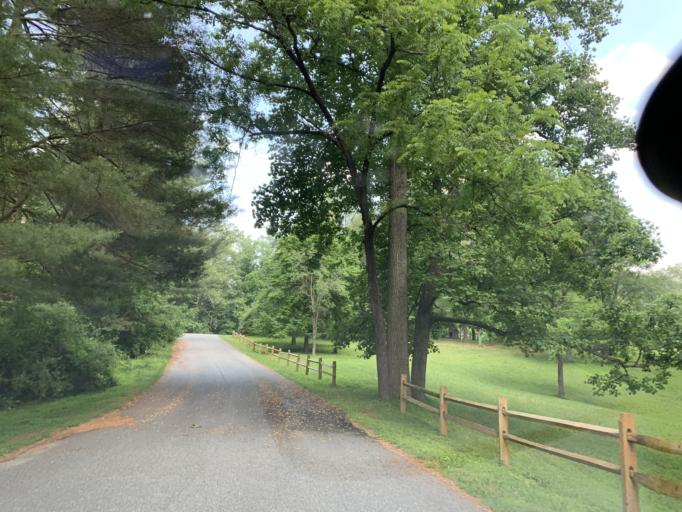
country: US
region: Maryland
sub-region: Carroll County
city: Eldersburg
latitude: 39.3557
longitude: -76.8834
